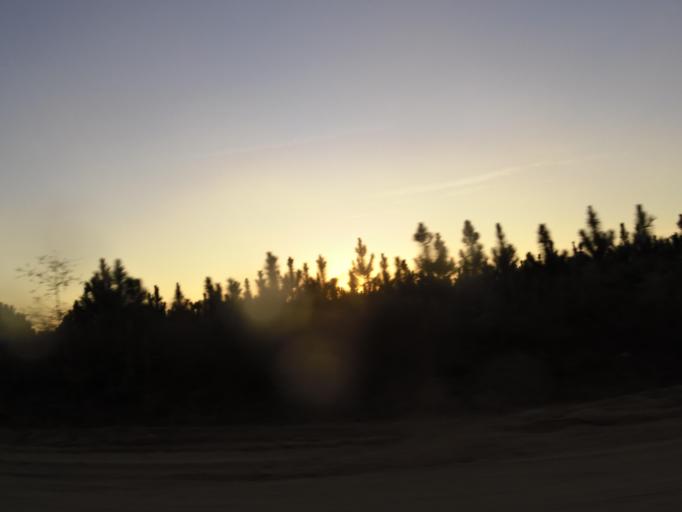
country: US
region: Florida
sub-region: Clay County
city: Green Cove Springs
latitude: 29.9134
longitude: -81.7806
